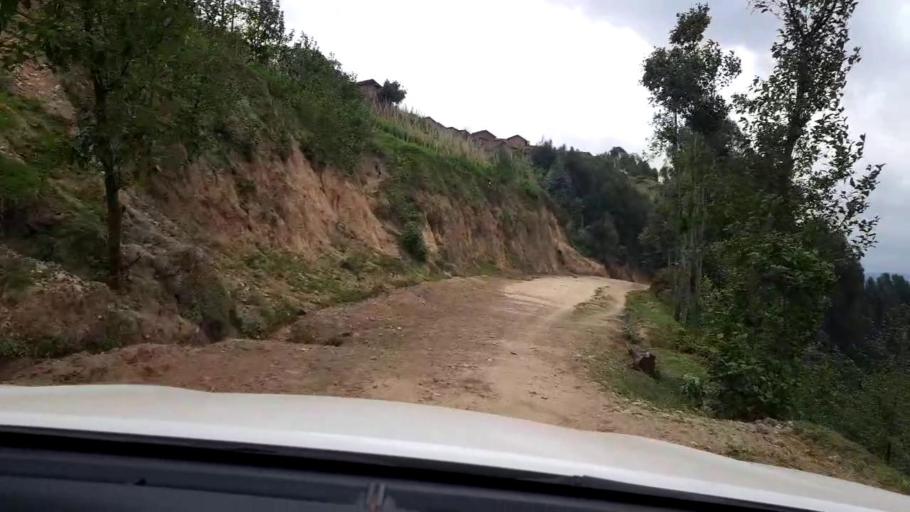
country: RW
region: Western Province
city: Kibuye
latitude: -1.8327
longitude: 29.5456
